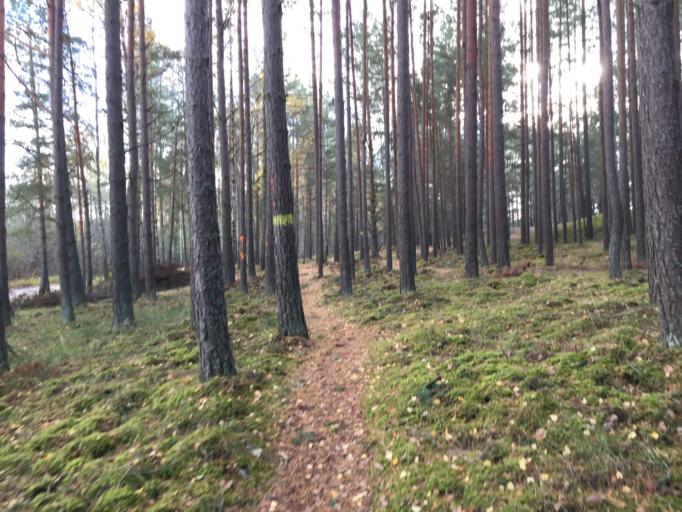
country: LV
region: Carnikava
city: Carnikava
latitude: 57.1480
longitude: 24.2633
